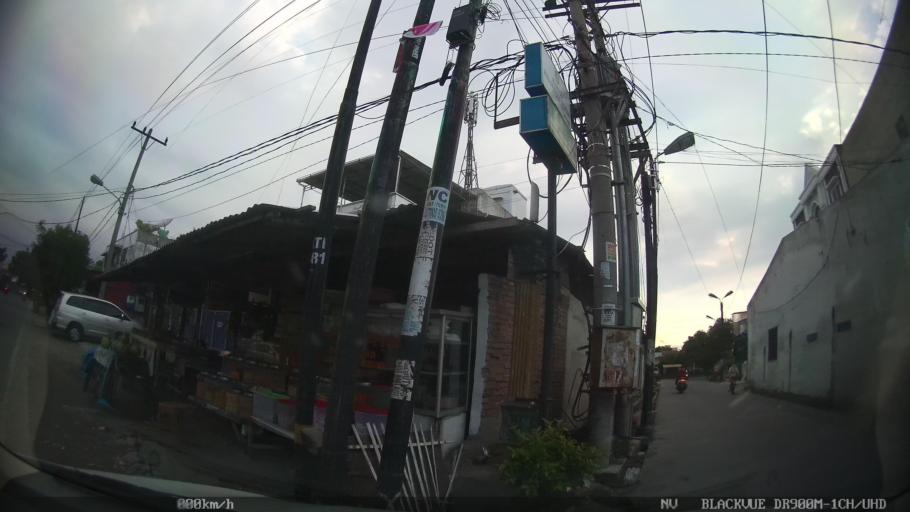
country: ID
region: North Sumatra
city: Medan
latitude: 3.6069
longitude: 98.6822
